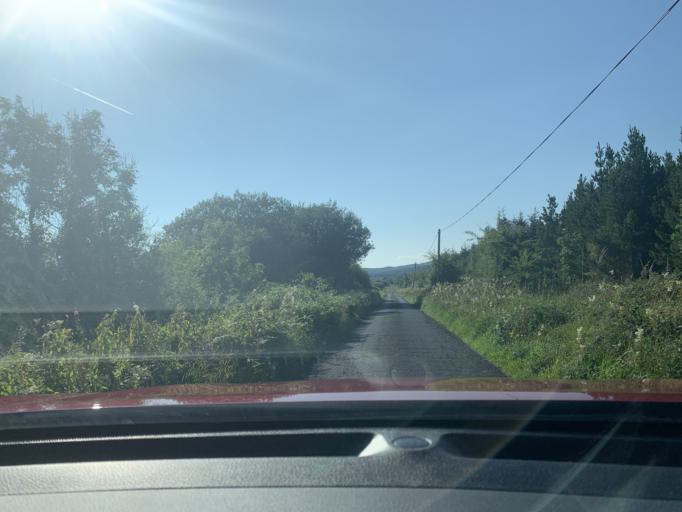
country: IE
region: Connaught
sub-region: Sligo
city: Tobercurry
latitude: 54.0762
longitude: -8.7903
